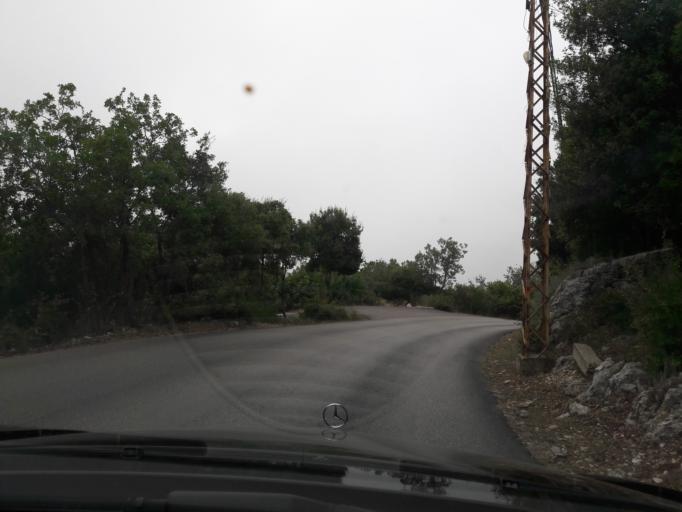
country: LB
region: Mont-Liban
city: Djounie
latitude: 33.9881
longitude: 35.6792
